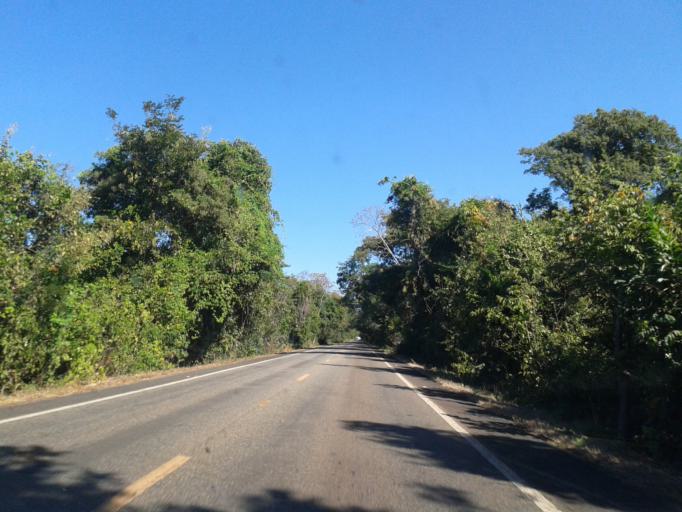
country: BR
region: Goias
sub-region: Crixas
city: Crixas
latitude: -14.0118
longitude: -50.3258
